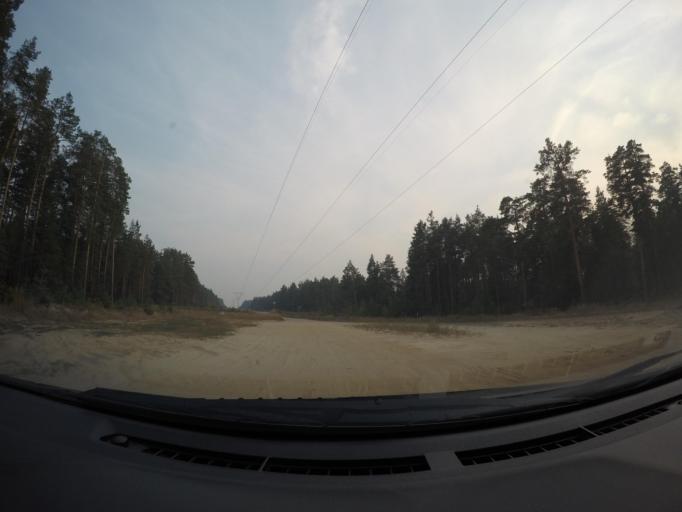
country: RU
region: Moskovskaya
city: Imeni Tsyurupy
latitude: 55.4975
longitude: 38.6882
